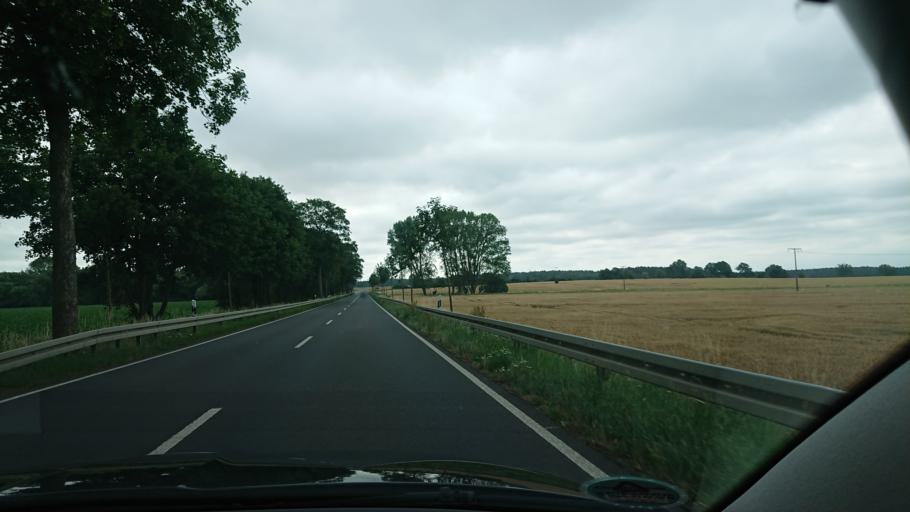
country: DE
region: Brandenburg
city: Plattenburg
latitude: 53.0137
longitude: 12.0159
